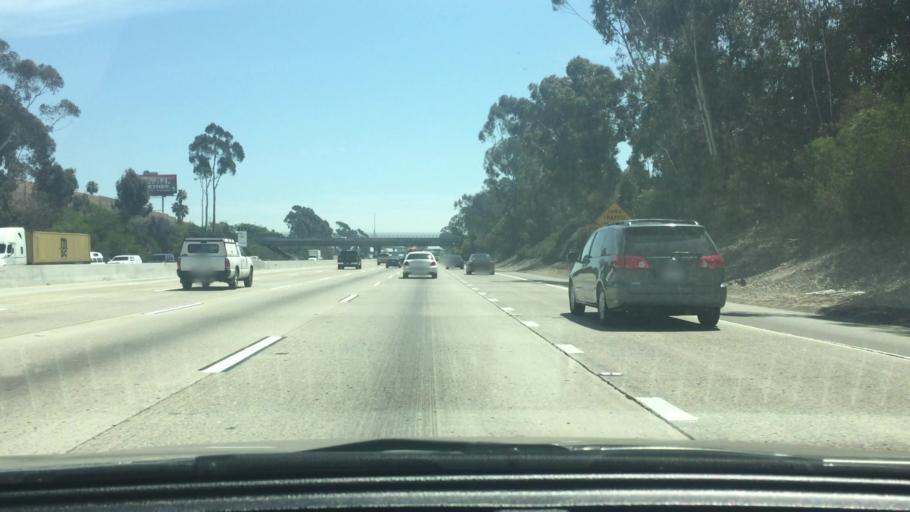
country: US
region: California
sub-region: San Diego County
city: National City
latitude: 32.6998
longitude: -117.0950
